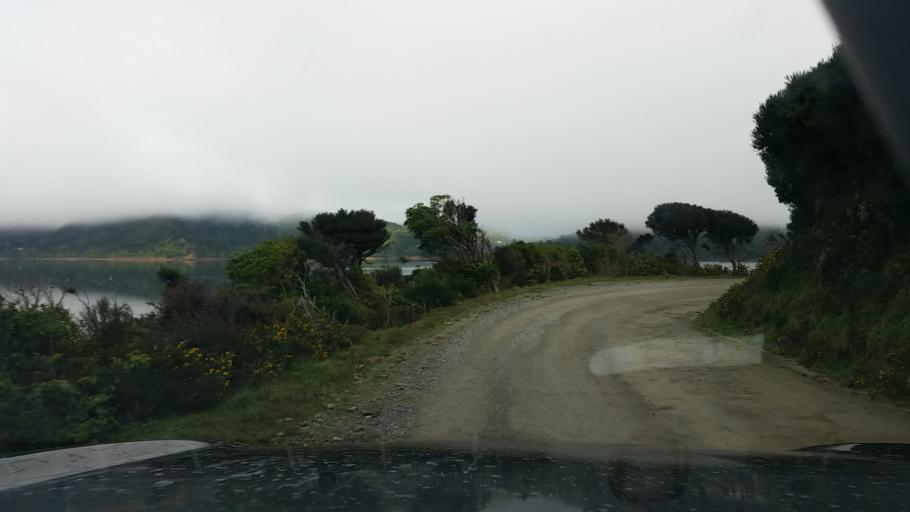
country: NZ
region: Marlborough
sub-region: Marlborough District
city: Picton
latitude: -41.1764
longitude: 174.0471
